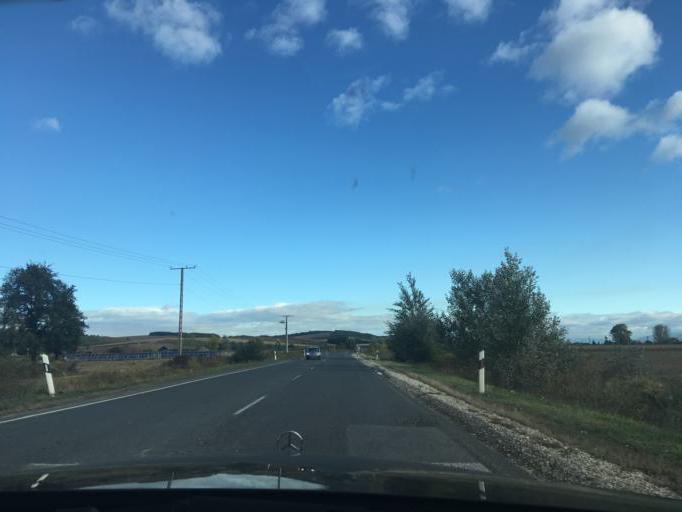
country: HU
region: Borsod-Abauj-Zemplen
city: Gonc
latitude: 48.4988
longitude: 21.2200
